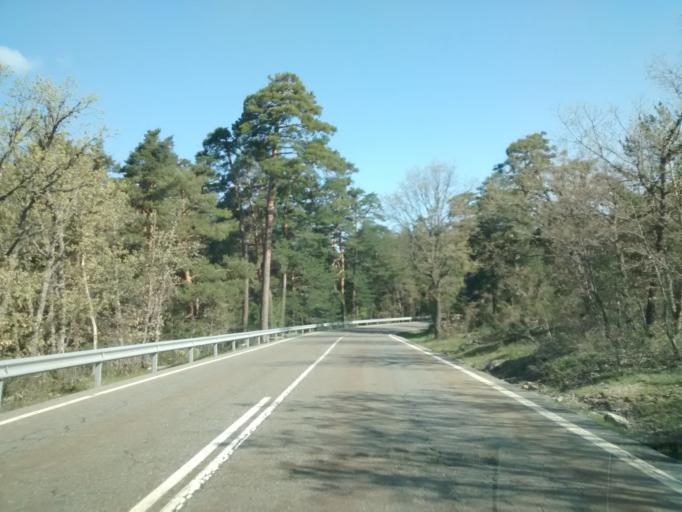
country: ES
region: Castille and Leon
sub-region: Provincia de Segovia
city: San Ildefonso
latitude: 40.8394
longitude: -4.0259
